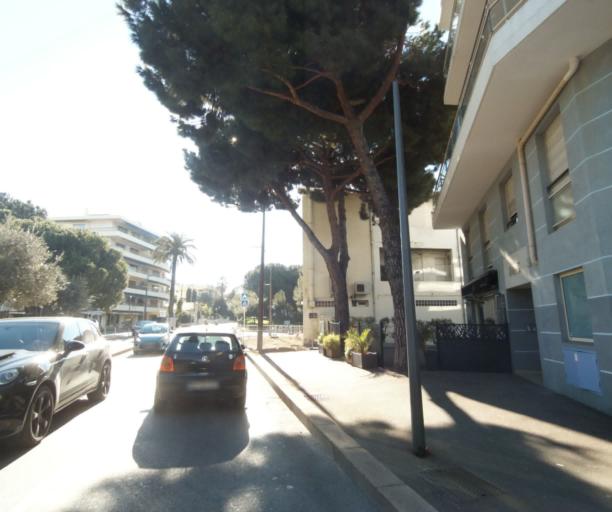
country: FR
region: Provence-Alpes-Cote d'Azur
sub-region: Departement des Alpes-Maritimes
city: Antibes
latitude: 43.5683
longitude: 7.1152
